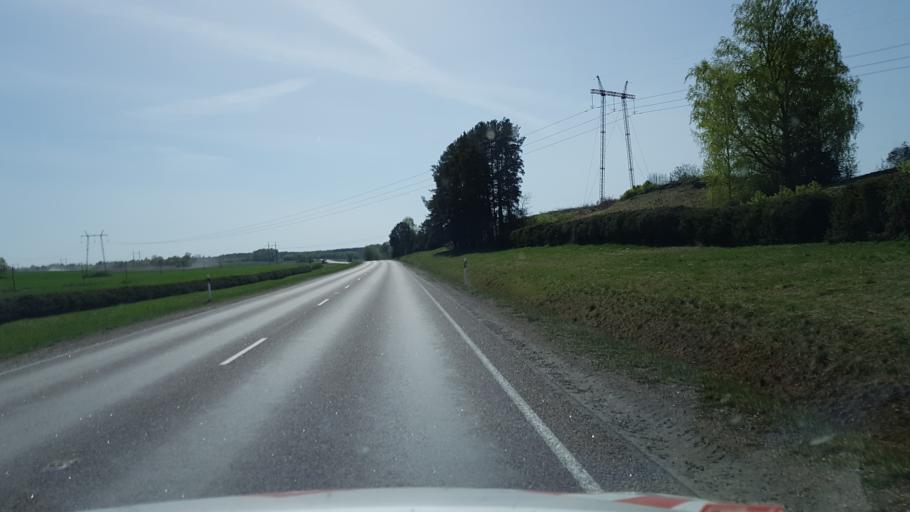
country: EE
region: Valgamaa
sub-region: Torva linn
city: Torva
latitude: 58.0346
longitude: 26.1796
